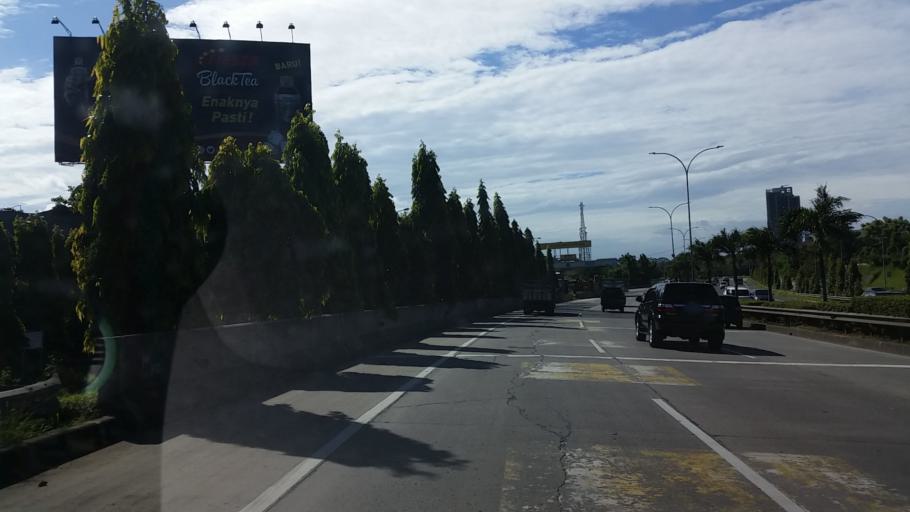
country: ID
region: Banten
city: South Tangerang
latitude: -6.2632
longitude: 106.7677
